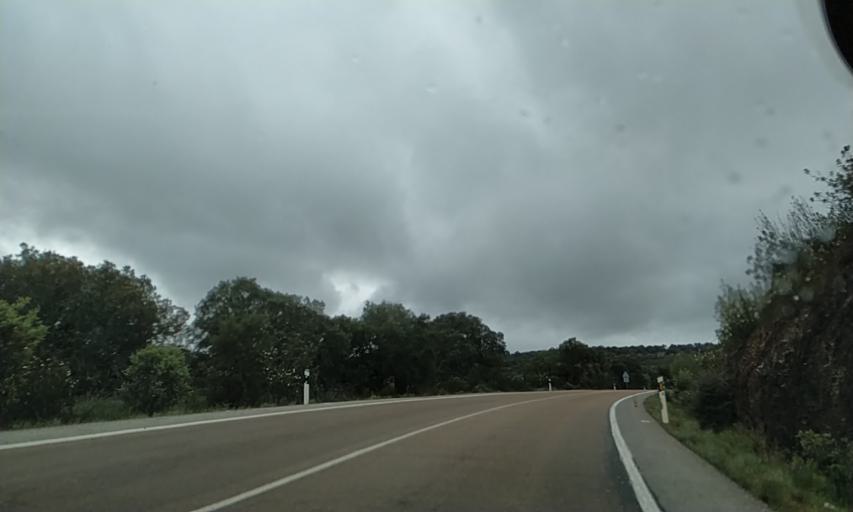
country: ES
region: Extremadura
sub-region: Provincia de Badajoz
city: Puebla de Obando
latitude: 39.2437
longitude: -6.5585
